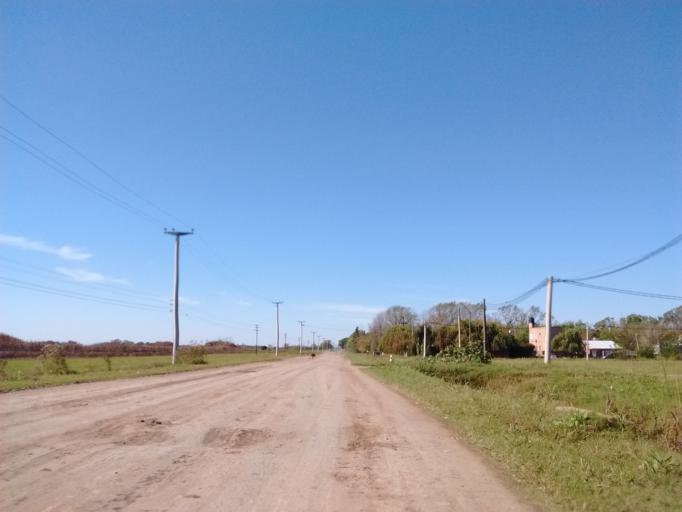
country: AR
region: Santa Fe
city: Funes
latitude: -32.9100
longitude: -60.8513
